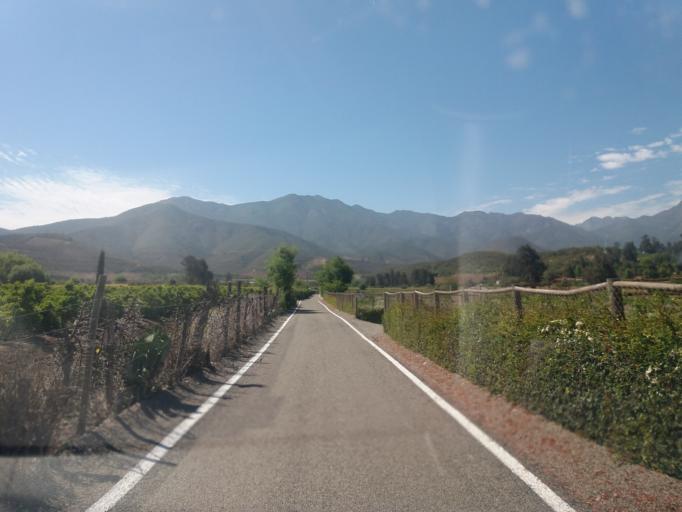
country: CL
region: Valparaiso
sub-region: Provincia de Quillota
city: Quillota
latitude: -32.8582
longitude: -71.2028
